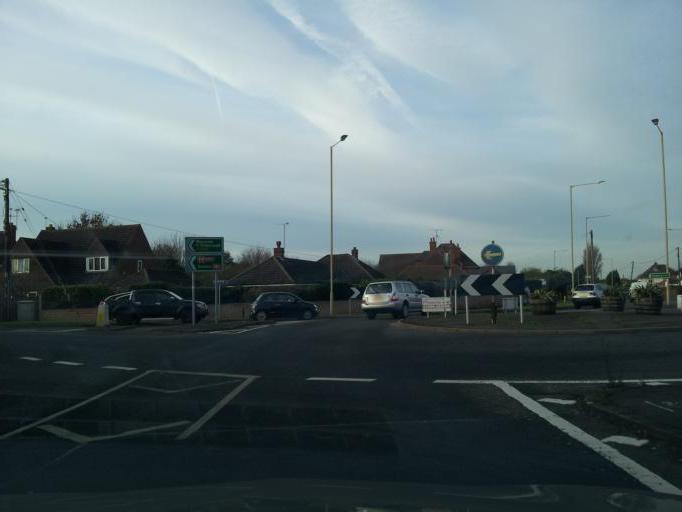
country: GB
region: England
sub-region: Buckinghamshire
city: Weston Turville
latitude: 51.7901
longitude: -0.7790
